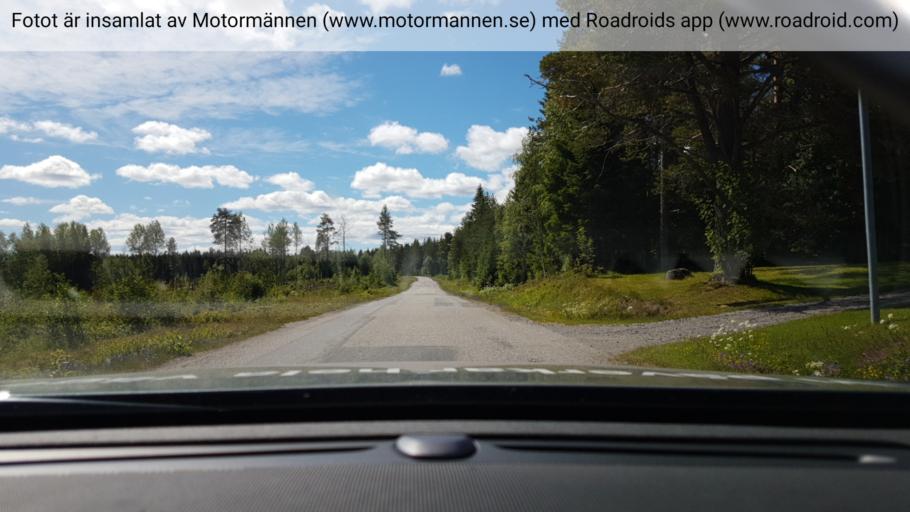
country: SE
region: Vaesterbotten
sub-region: Skelleftea Kommun
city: Burea
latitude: 64.4533
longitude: 21.3567
